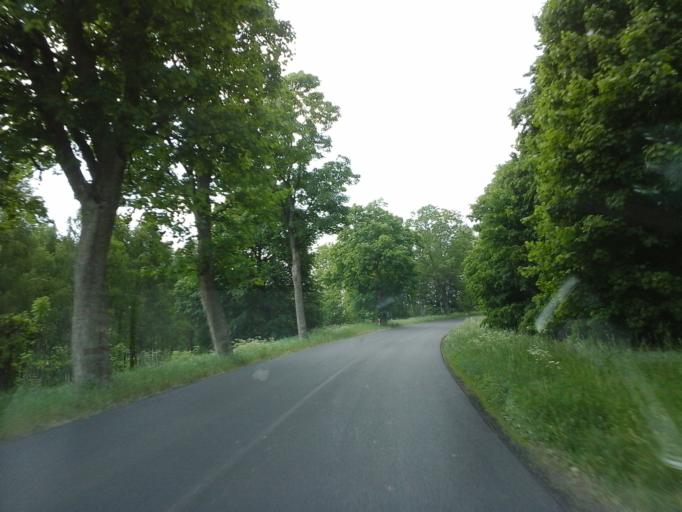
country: PL
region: West Pomeranian Voivodeship
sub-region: Powiat choszczenski
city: Recz
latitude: 53.1904
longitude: 15.6387
